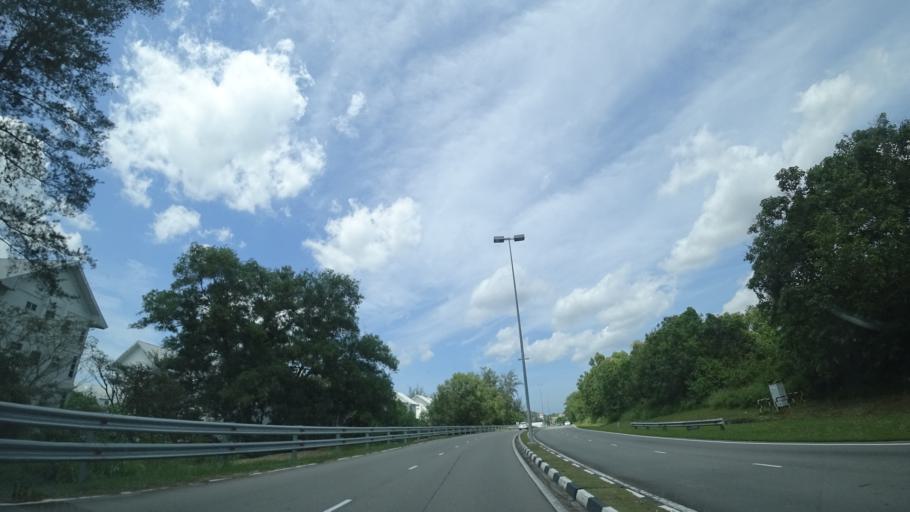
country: BN
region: Brunei and Muara
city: Bandar Seri Begawan
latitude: 4.9007
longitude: 114.9099
